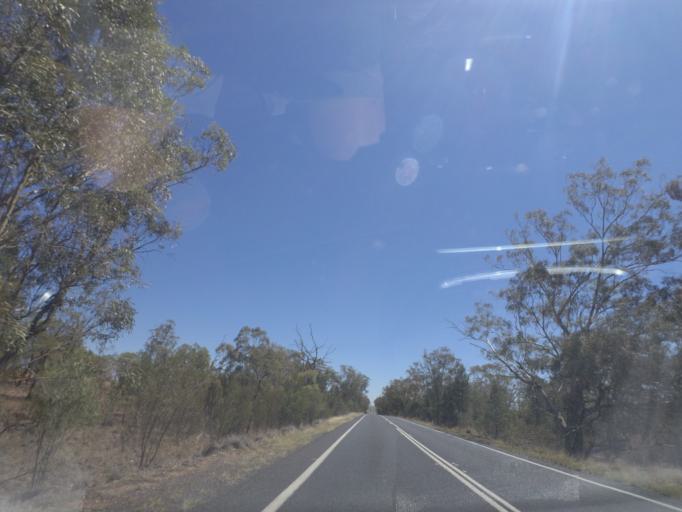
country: AU
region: New South Wales
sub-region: Gilgandra
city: Gilgandra
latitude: -31.4818
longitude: 148.8862
